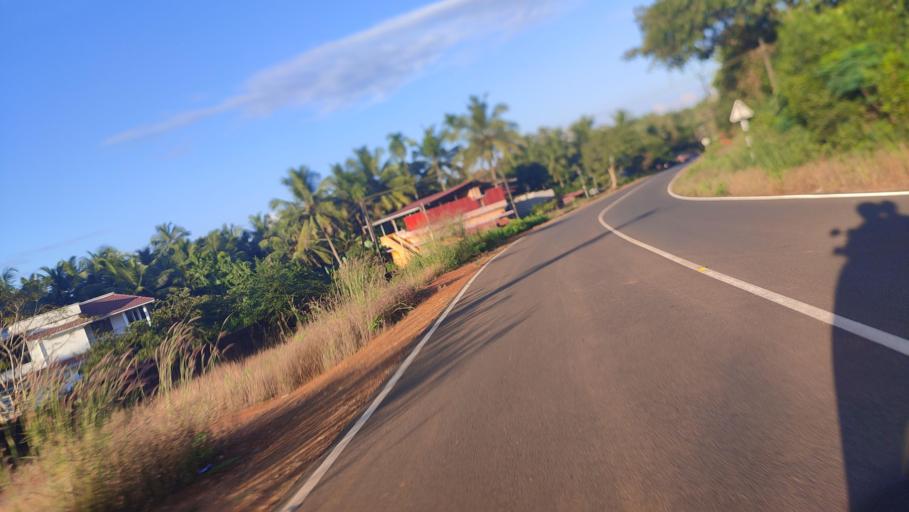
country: IN
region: Kerala
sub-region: Kasaragod District
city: Kasaragod
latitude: 12.4637
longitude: 75.0707
